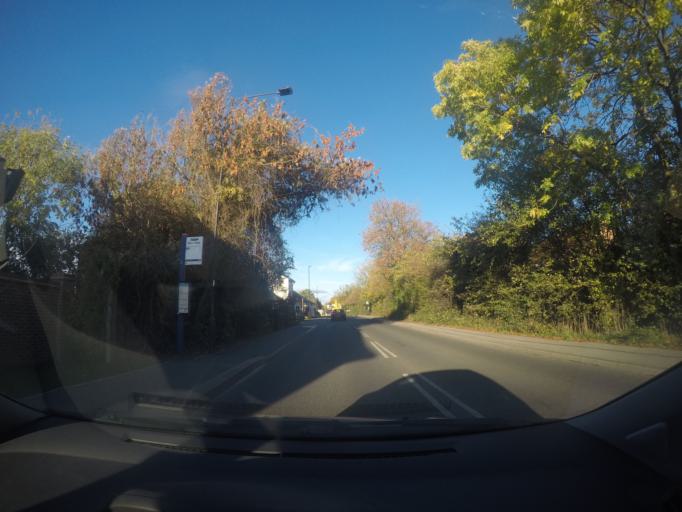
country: GB
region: England
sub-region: City of York
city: York
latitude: 53.9817
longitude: -1.0947
